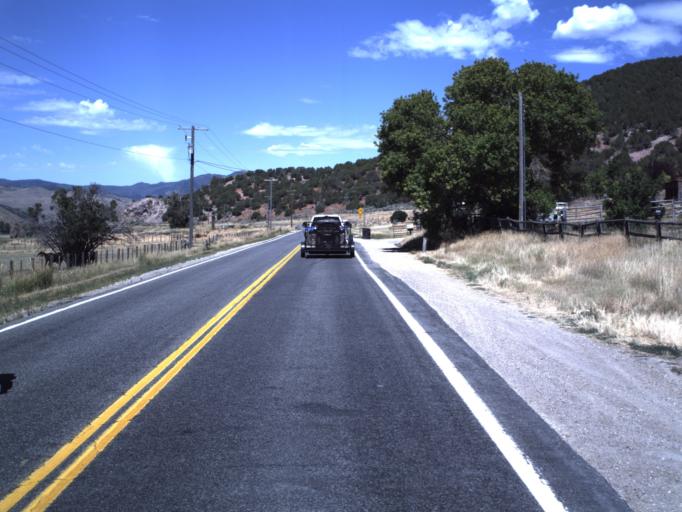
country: US
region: Utah
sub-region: Summit County
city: Oakley
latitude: 40.7389
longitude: -111.3508
